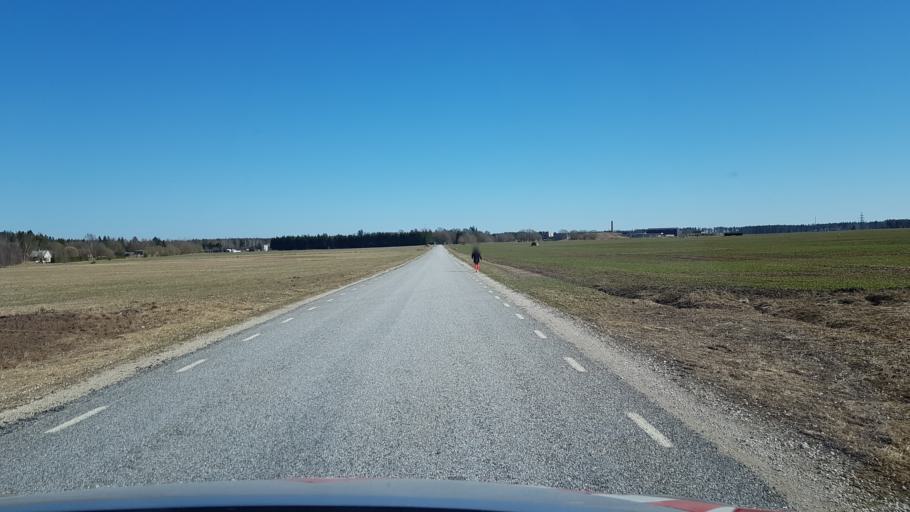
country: EE
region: Laeaene-Virumaa
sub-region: Viru-Nigula vald
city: Kunda
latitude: 59.4004
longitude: 26.5502
